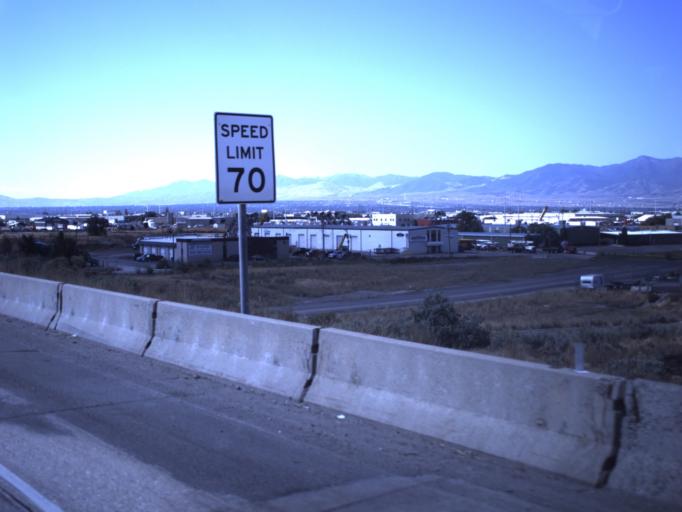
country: US
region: Utah
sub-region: Salt Lake County
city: Salt Lake City
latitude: 40.7529
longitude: -111.9488
